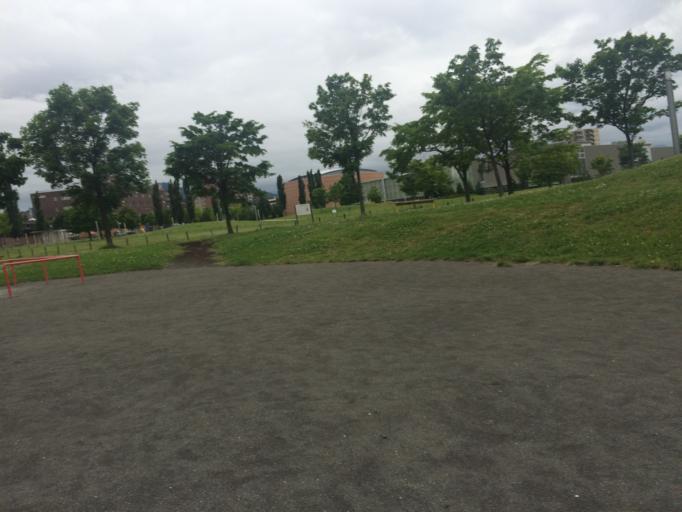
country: JP
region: Hokkaido
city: Sapporo
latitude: 43.0573
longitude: 141.3915
